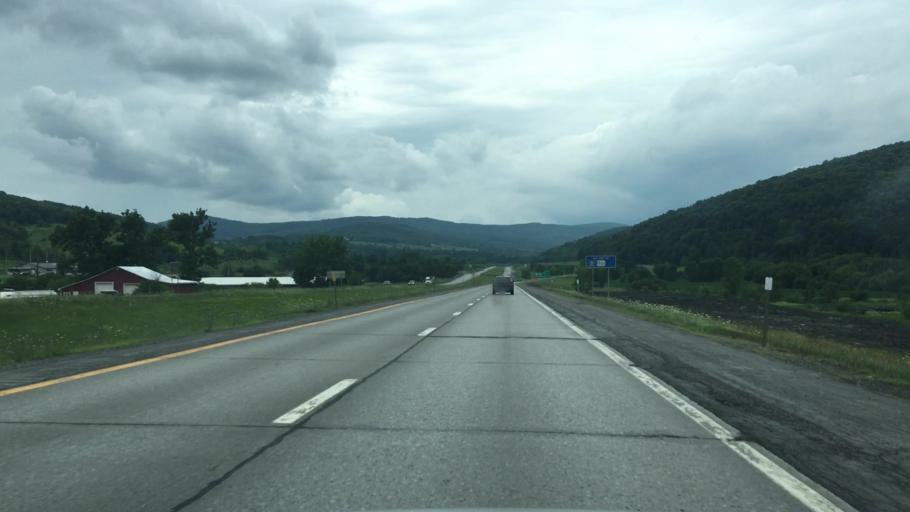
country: US
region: New York
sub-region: Schoharie County
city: Cobleskill
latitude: 42.6456
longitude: -74.5342
